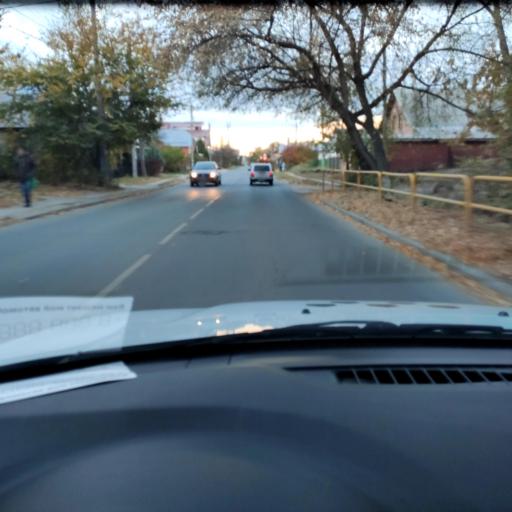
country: RU
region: Samara
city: Tol'yatti
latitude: 53.5330
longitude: 49.4106
